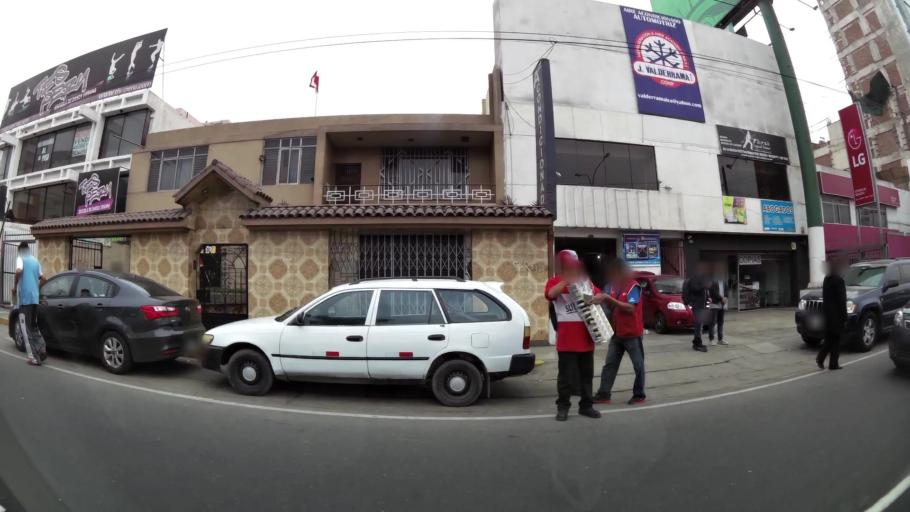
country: PE
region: Callao
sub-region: Callao
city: Callao
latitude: -12.0767
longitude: -77.0950
